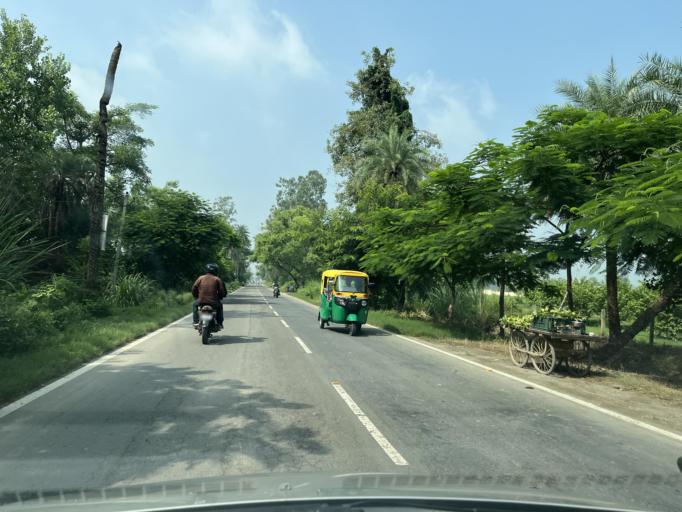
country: IN
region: Uttarakhand
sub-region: Udham Singh Nagar
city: Bazpur
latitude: 29.1741
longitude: 79.1702
